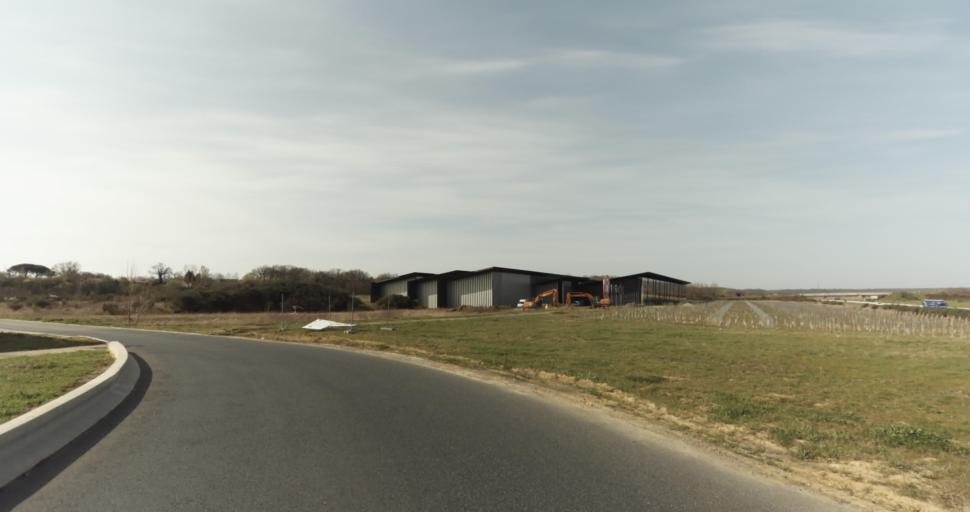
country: FR
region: Midi-Pyrenees
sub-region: Departement de la Haute-Garonne
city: Buzet-sur-Tarn
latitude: 43.7528
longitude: 1.6554
